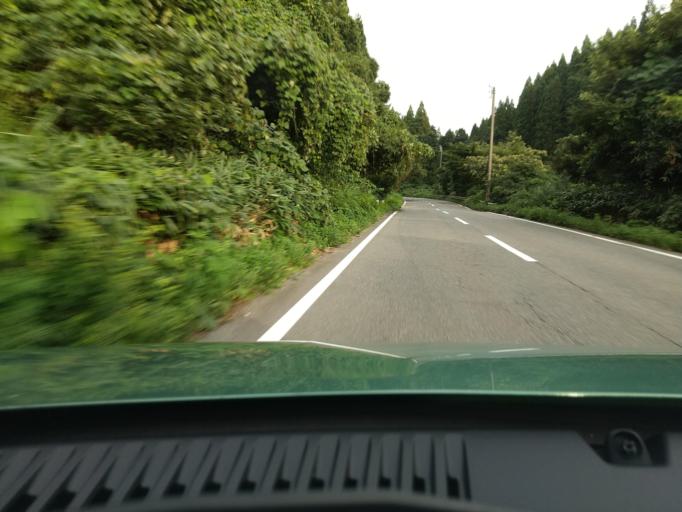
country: JP
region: Akita
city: Akita
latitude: 39.7349
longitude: 140.1737
